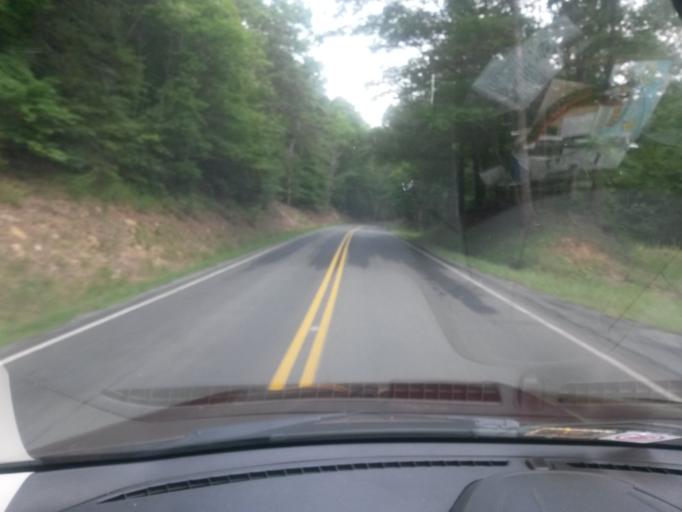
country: US
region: Virginia
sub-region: Bath County
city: Warm Springs
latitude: 38.0765
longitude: -79.7796
